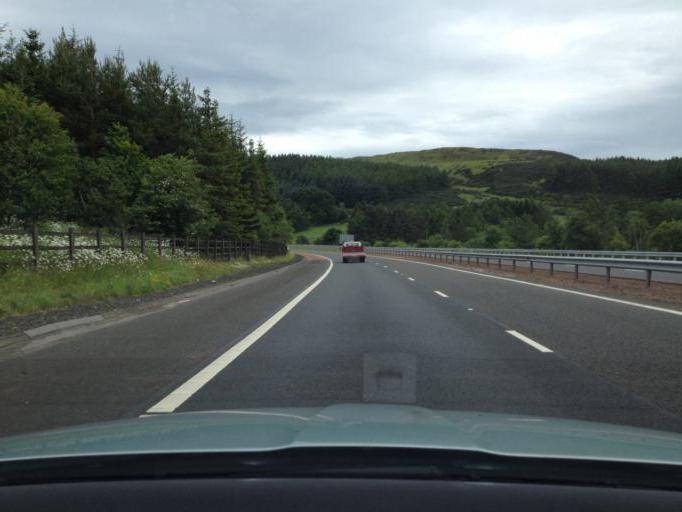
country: GB
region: Scotland
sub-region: Perth and Kinross
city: Bridge of Earn
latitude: 56.3253
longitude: -3.3972
